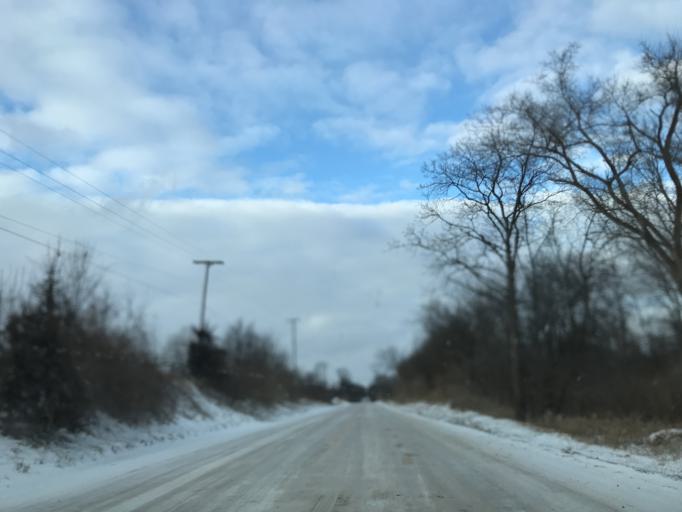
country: US
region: Michigan
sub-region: Oakland County
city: South Lyon
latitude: 42.4346
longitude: -83.5908
